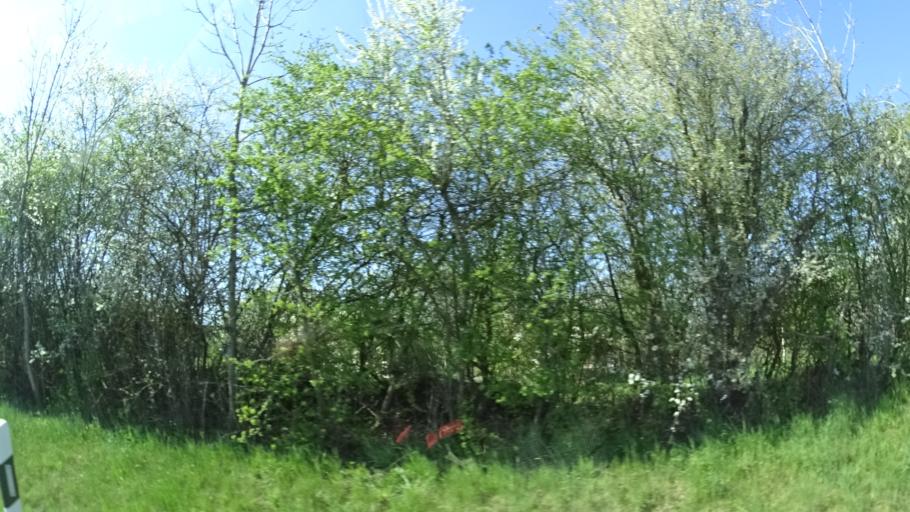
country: DE
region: Bavaria
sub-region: Upper Palatinate
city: Edelsfeld
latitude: 49.5451
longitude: 11.7237
